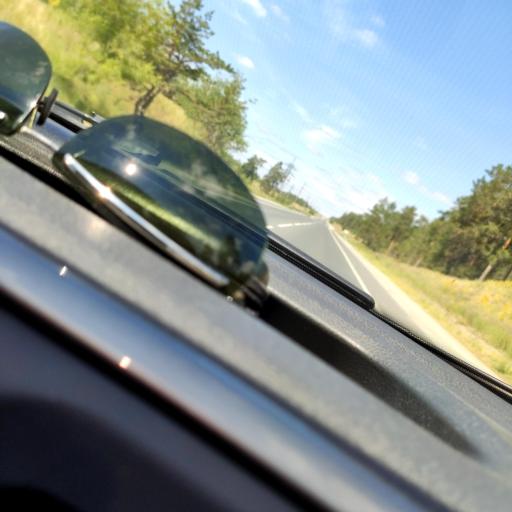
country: RU
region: Samara
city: Volzhskiy
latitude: 53.4466
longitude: 50.0990
